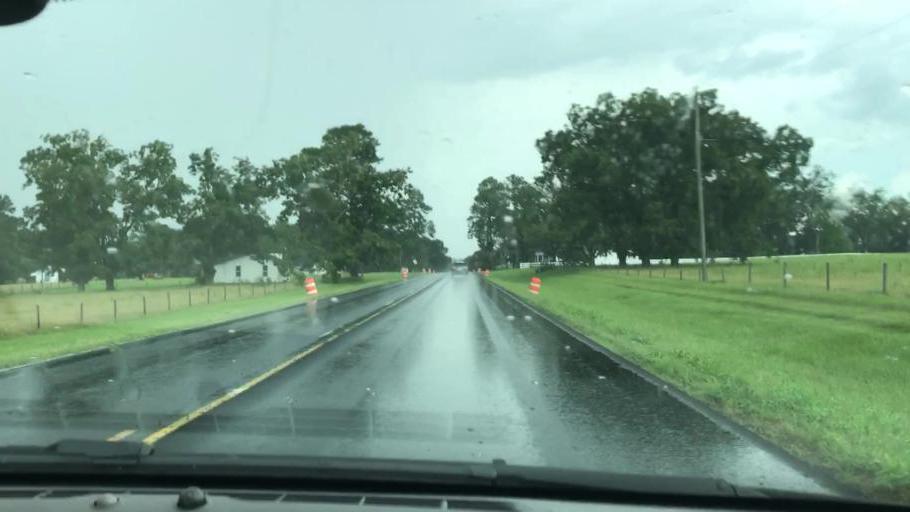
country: US
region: Georgia
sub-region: Clay County
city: Fort Gaines
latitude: 31.5415
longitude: -85.0204
